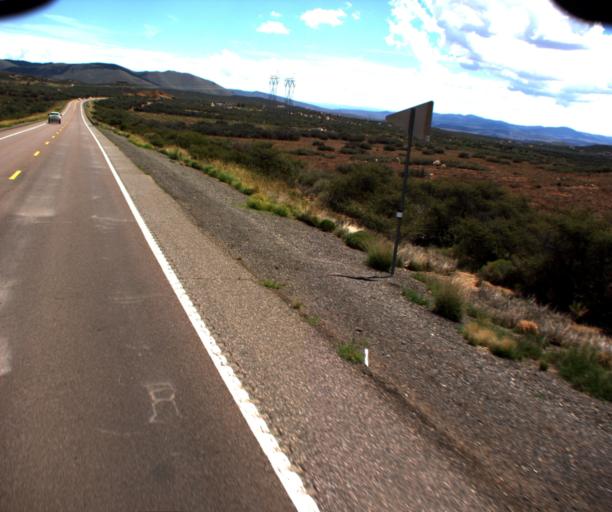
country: US
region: Arizona
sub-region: Yavapai County
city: Dewey-Humboldt
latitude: 34.5456
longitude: -112.1789
